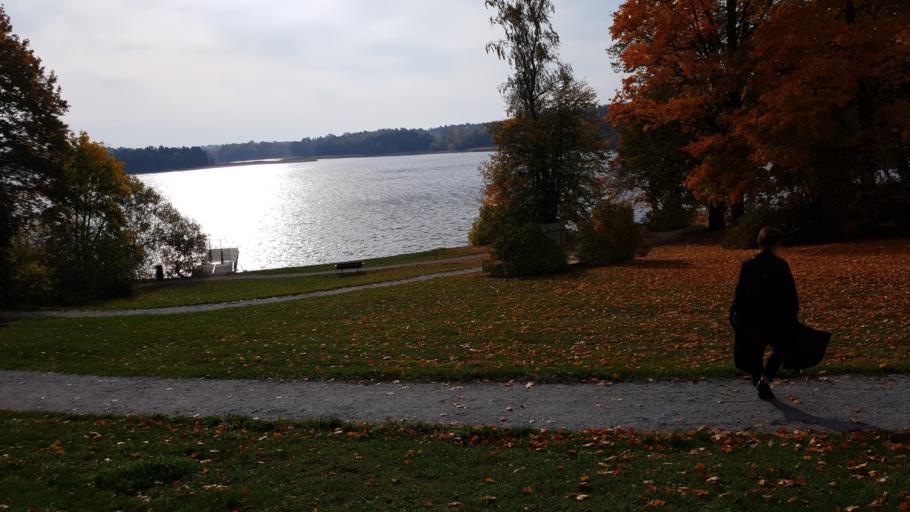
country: SE
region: Stockholm
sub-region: Stockholms Kommun
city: Bromma
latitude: 59.3404
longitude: 17.8774
